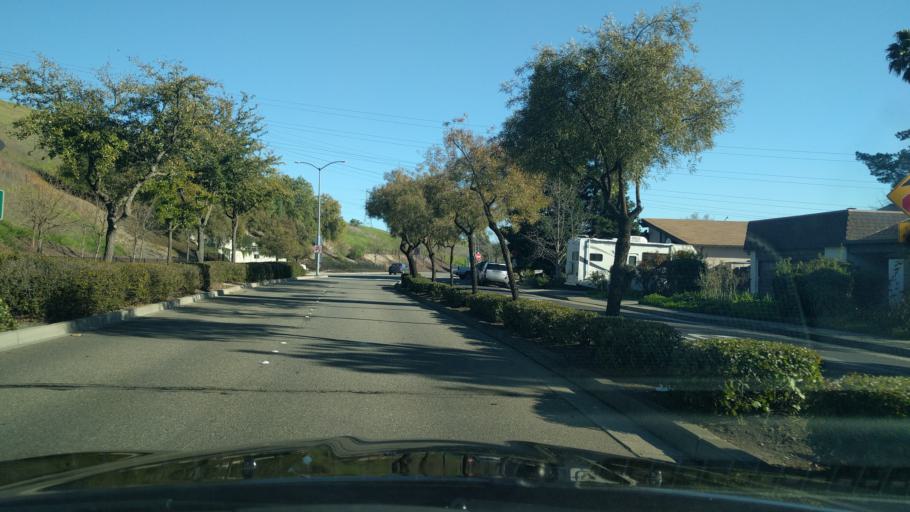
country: US
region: California
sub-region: Alameda County
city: Dublin
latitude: 37.7484
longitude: -121.9337
